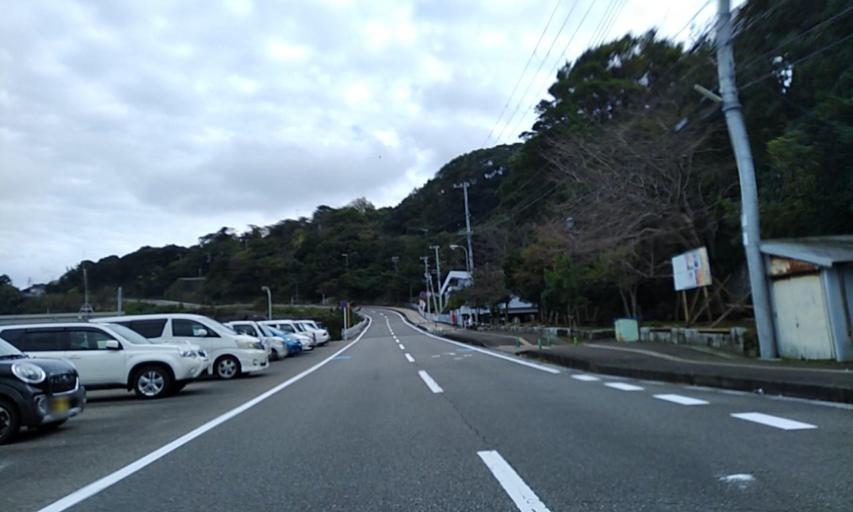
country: JP
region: Wakayama
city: Shingu
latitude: 33.5900
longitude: 135.9472
